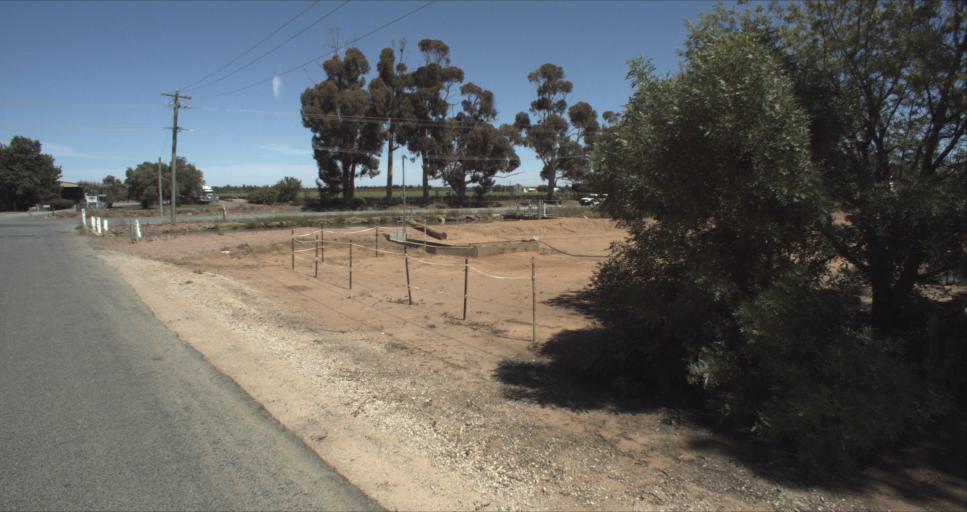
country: AU
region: New South Wales
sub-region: Leeton
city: Leeton
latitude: -34.5509
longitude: 146.3724
